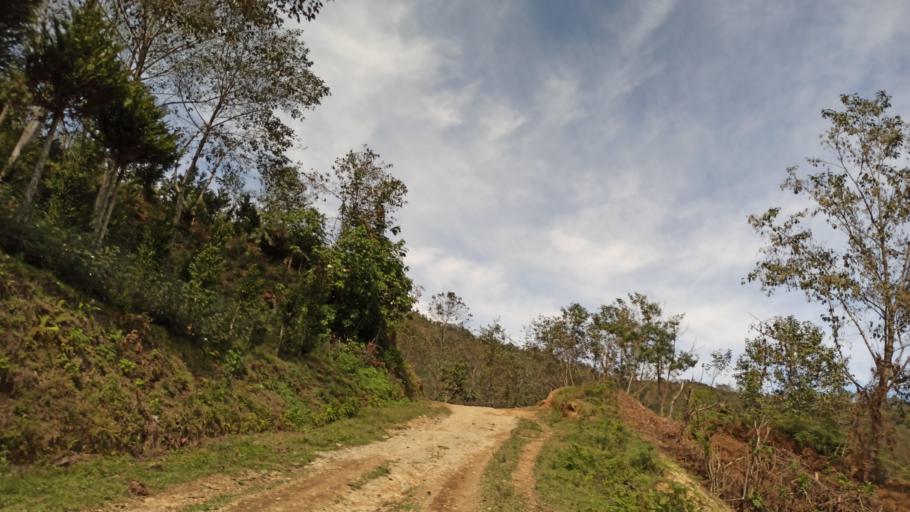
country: MX
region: Veracruz
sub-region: La Perla
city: Metlac Hernandez (Metlac Primero)
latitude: 18.9732
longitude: -97.1047
